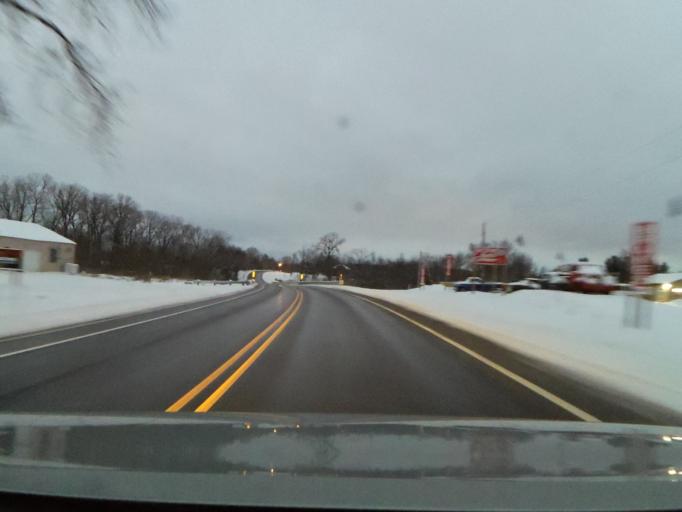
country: US
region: Wisconsin
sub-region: Dunn County
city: Menomonie
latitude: 44.9280
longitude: -91.9892
